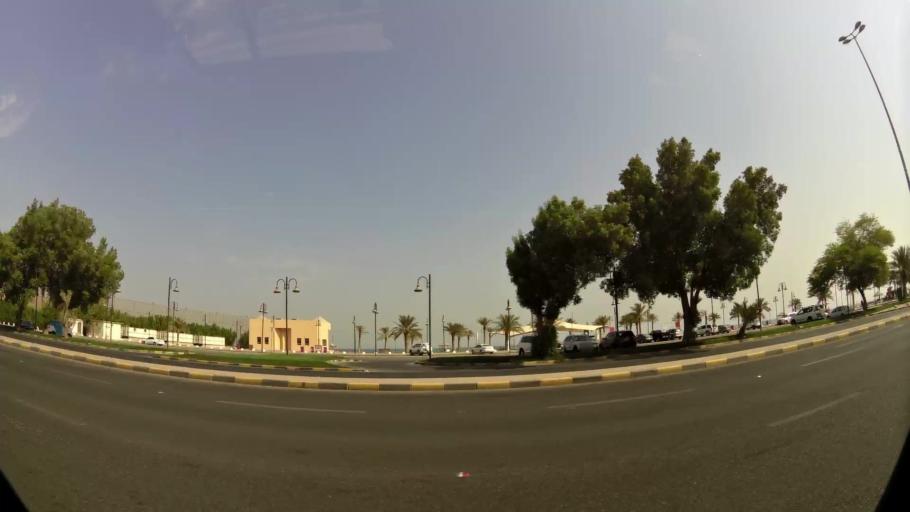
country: KW
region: Al Ahmadi
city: Al Fintas
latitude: 29.1786
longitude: 48.1210
